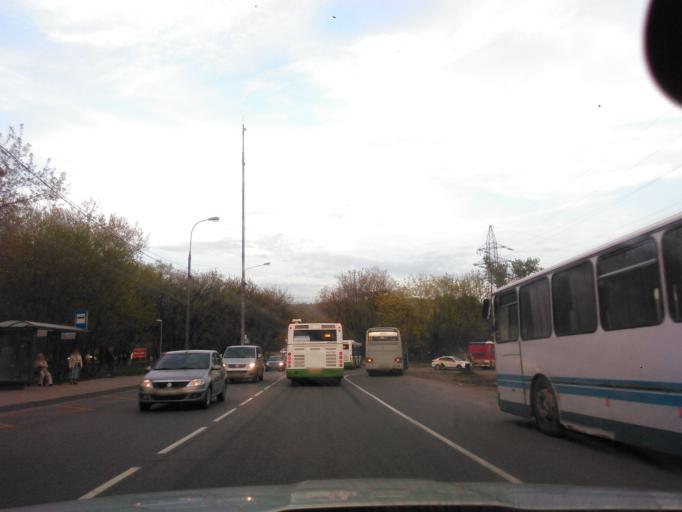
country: RU
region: Moscow
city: Kuz'minki
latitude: 55.6732
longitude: 37.8049
